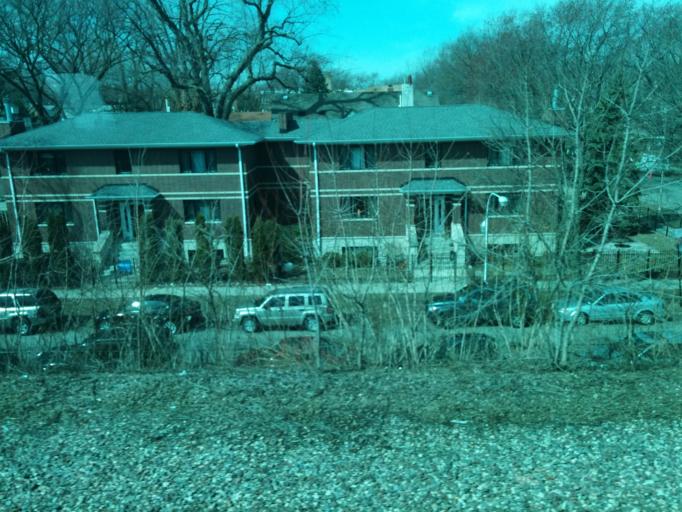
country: US
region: Illinois
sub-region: Cook County
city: Evanston
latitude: 42.0087
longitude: -87.6757
